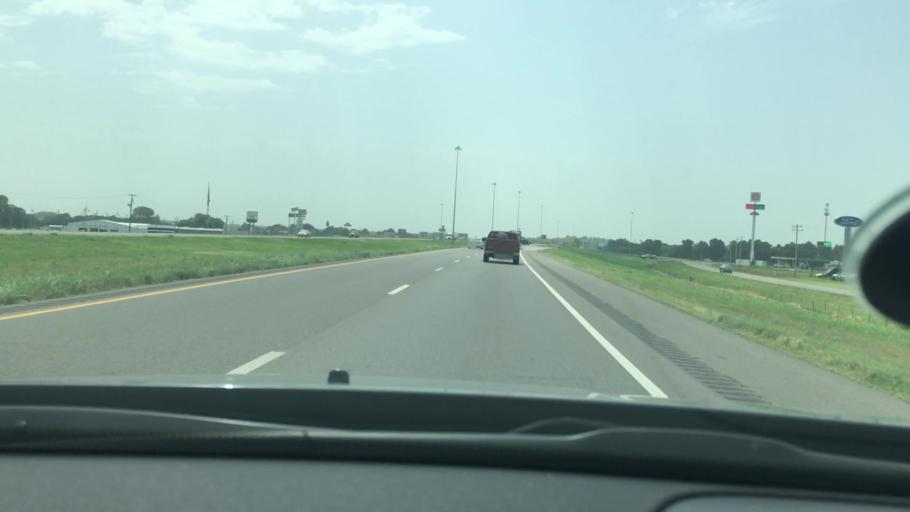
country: US
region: Oklahoma
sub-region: Garvin County
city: Pauls Valley
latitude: 34.7446
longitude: -97.2683
